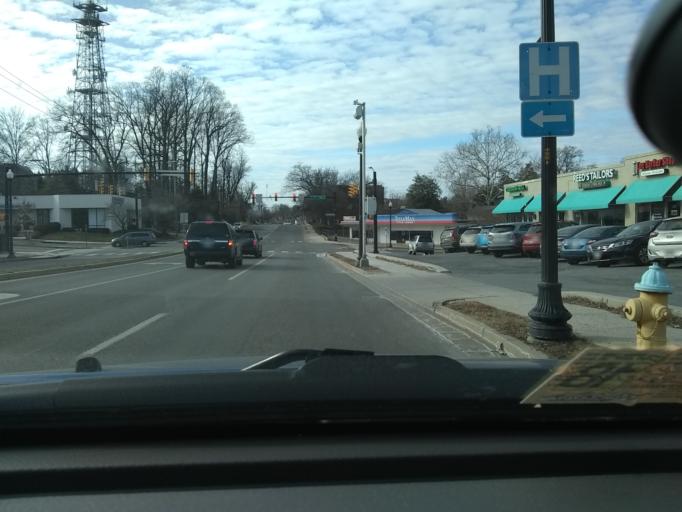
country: US
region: Virginia
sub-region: Arlington County
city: Arlington
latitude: 38.8964
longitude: -77.1326
